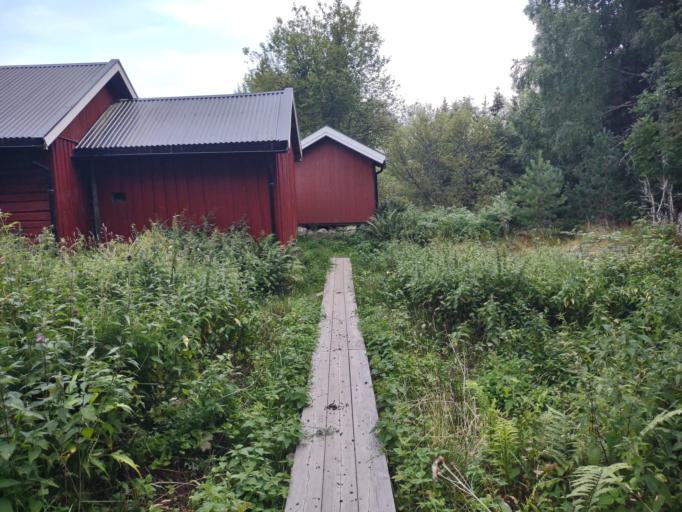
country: NO
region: Akershus
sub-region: Enebakk
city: Flateby
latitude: 59.8156
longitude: 11.0440
